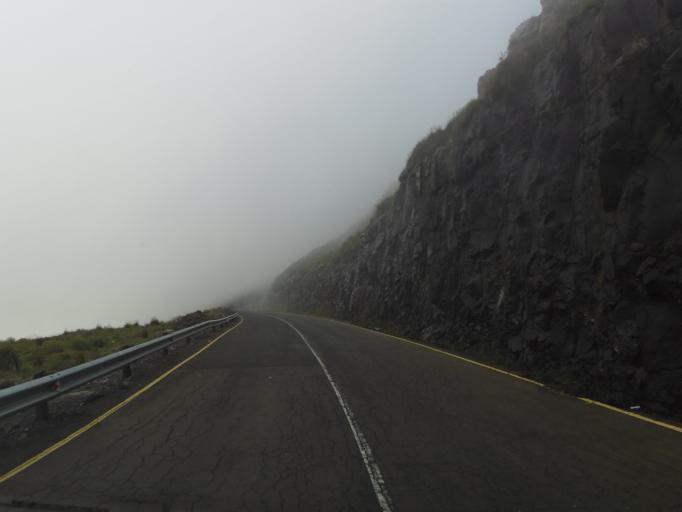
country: LS
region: Butha-Buthe
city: Butha-Buthe
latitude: -29.0633
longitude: 28.4058
